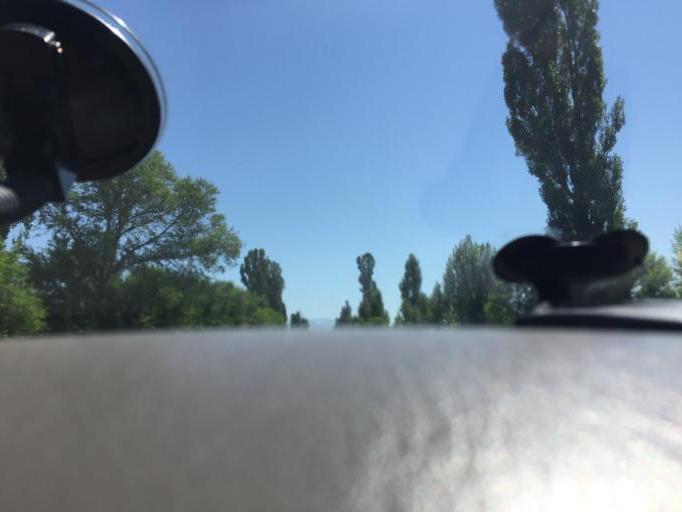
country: KG
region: Ysyk-Koel
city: Tyup
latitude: 42.7447
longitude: 78.4162
